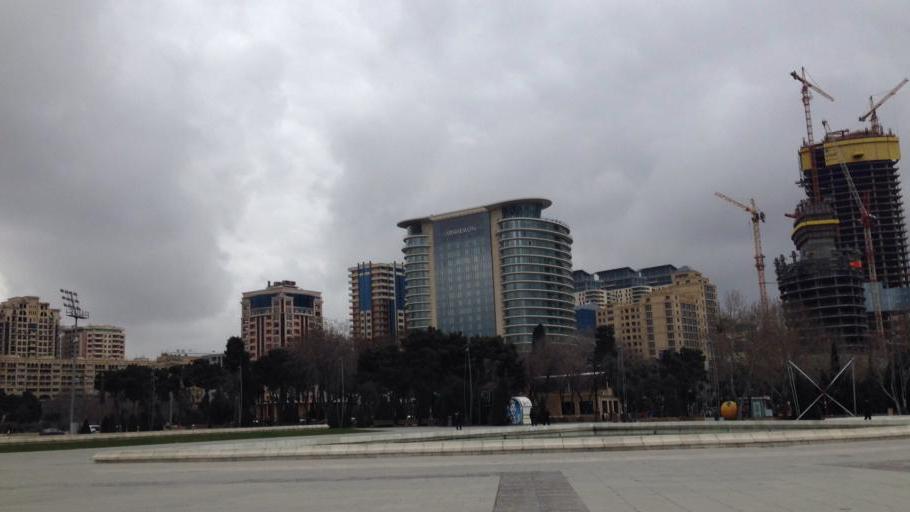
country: AZ
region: Baki
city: Baku
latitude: 40.3715
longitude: 49.8533
